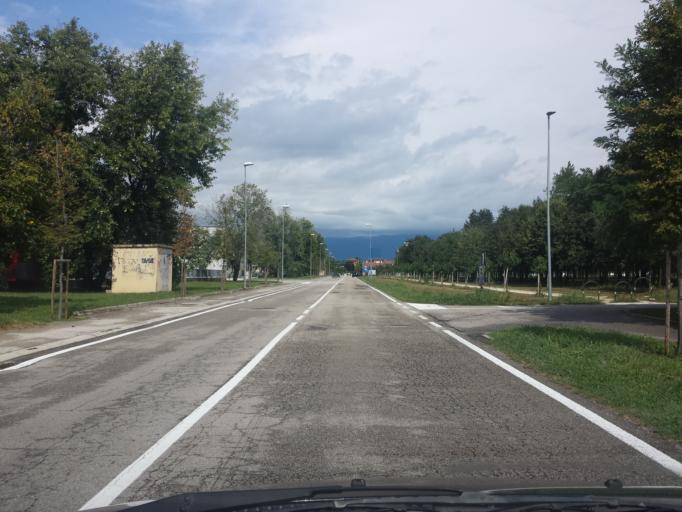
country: IT
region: Veneto
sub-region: Provincia di Padova
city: Galliera Veneta
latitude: 45.6731
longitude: 11.8165
